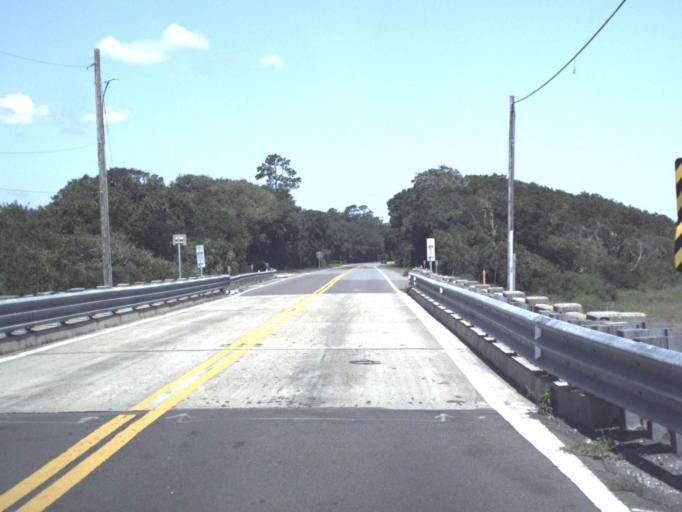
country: US
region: Florida
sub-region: Duval County
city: Atlantic Beach
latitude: 30.4632
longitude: -81.4312
